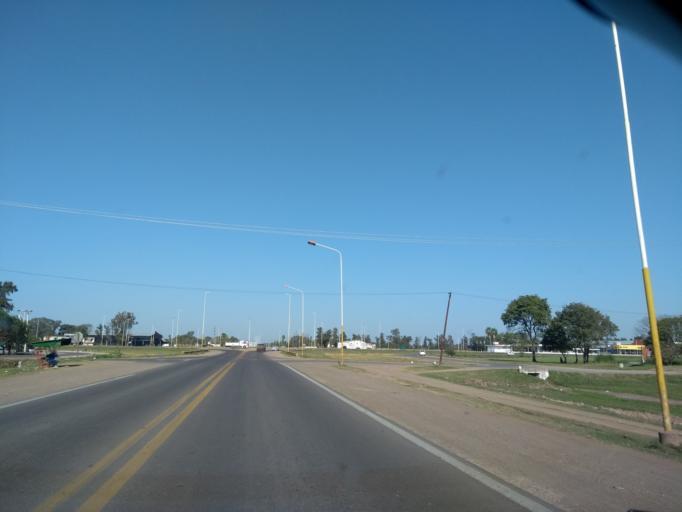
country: AR
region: Chaco
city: Presidencia Roque Saenz Pena
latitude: -26.8099
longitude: -60.4173
